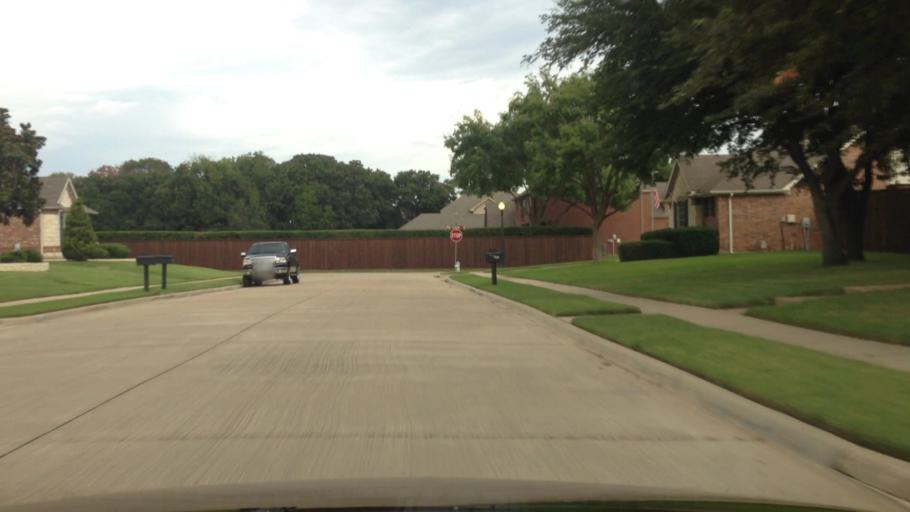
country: US
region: Texas
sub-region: Dallas County
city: Coppell
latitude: 33.0040
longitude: -97.0413
